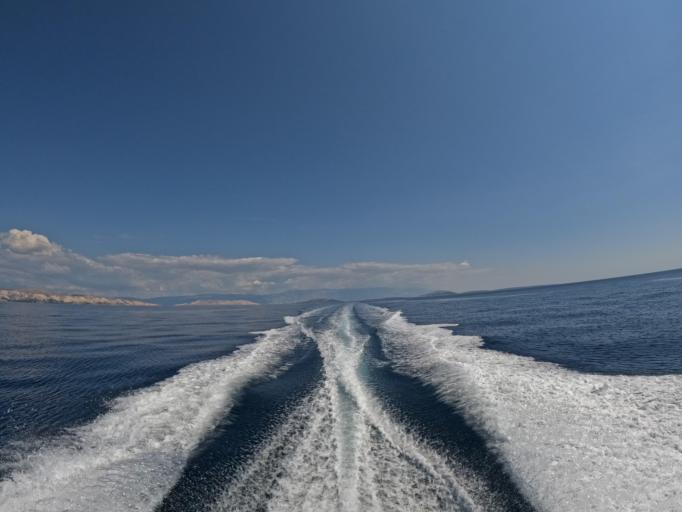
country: HR
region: Primorsko-Goranska
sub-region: Grad Krk
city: Krk
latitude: 44.9183
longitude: 14.5718
